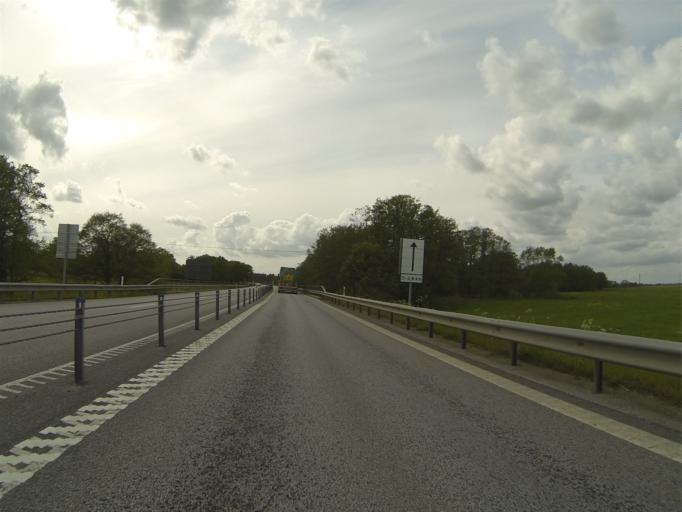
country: SE
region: Skane
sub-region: Lunds Kommun
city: Veberod
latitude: 55.6411
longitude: 13.5382
